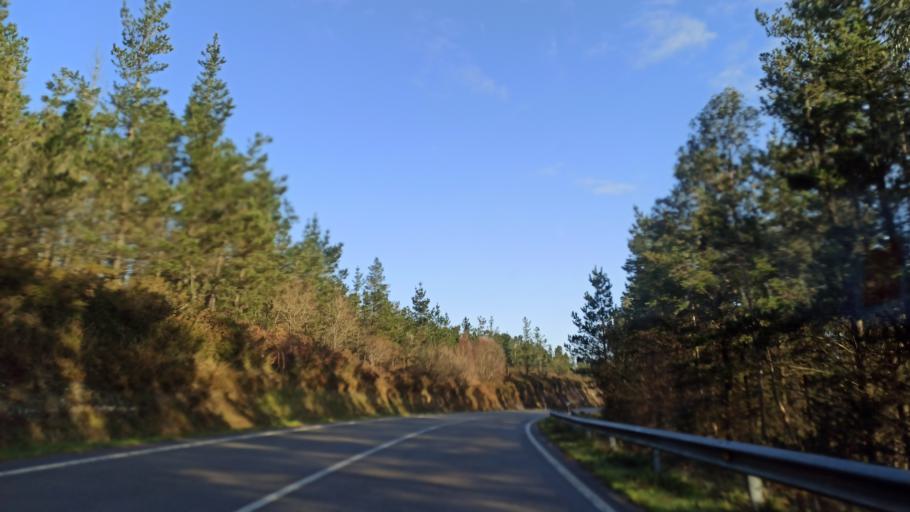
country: ES
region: Galicia
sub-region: Provincia da Coruna
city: As Pontes de Garcia Rodriguez
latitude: 43.4918
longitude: -7.8346
